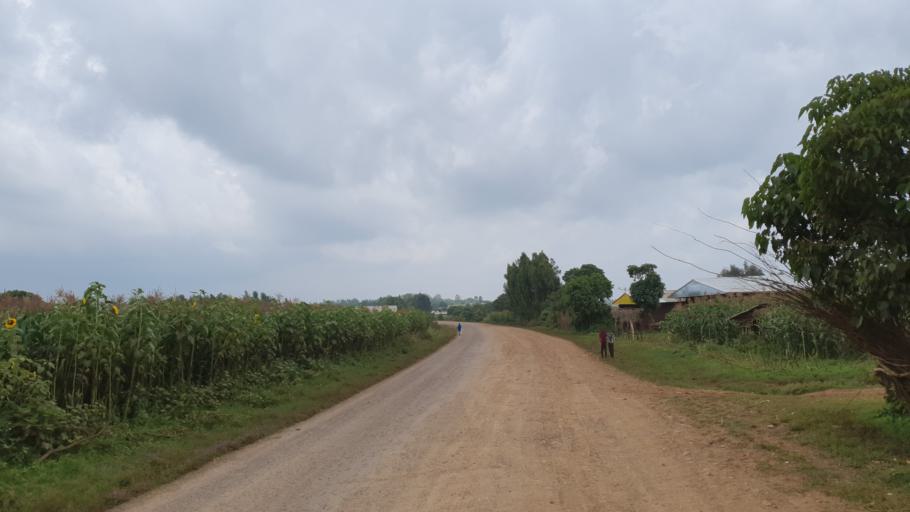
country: ET
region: Amhara
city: Bure
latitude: 10.6086
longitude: 37.0385
